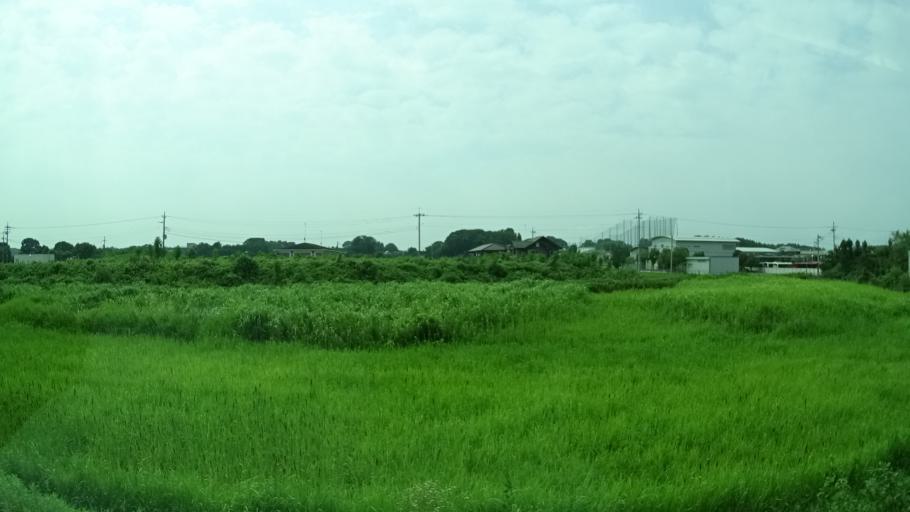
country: JP
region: Tochigi
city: Mashiko
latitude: 36.4595
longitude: 140.0870
